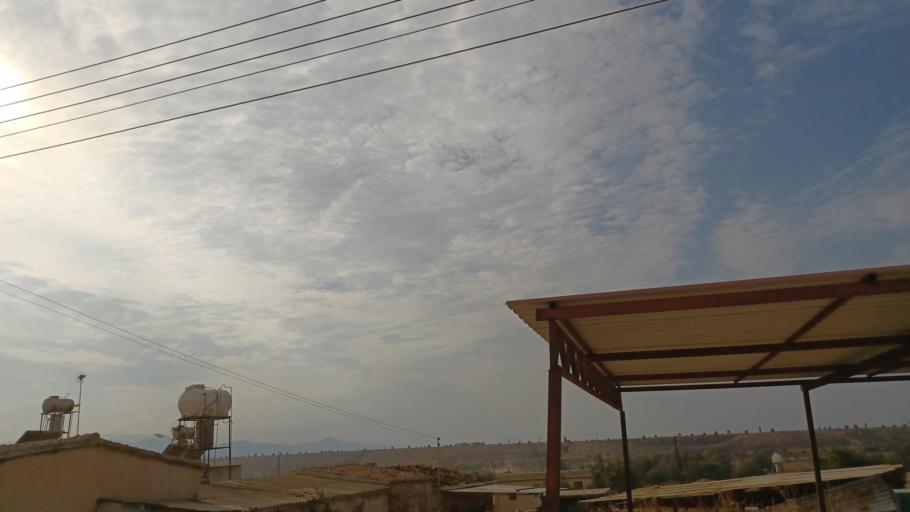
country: CY
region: Lefkosia
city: Peristerona
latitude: 35.0993
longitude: 33.0940
